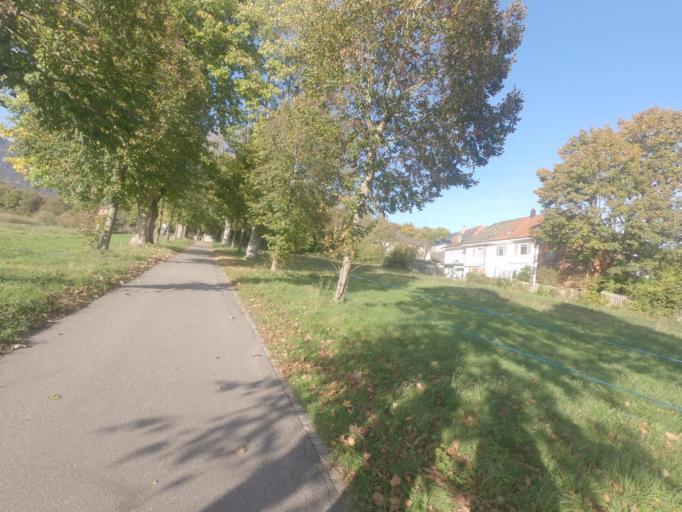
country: CH
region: Solothurn
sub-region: Bezirk Solothurn
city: Solothurn
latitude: 47.2183
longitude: 7.5284
